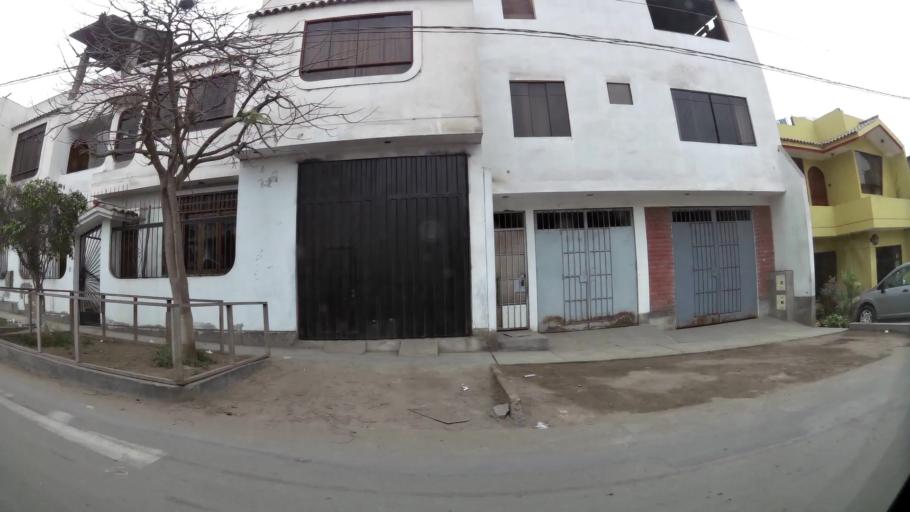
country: PE
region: Lima
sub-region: Lima
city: Surco
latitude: -12.1974
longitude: -76.9612
